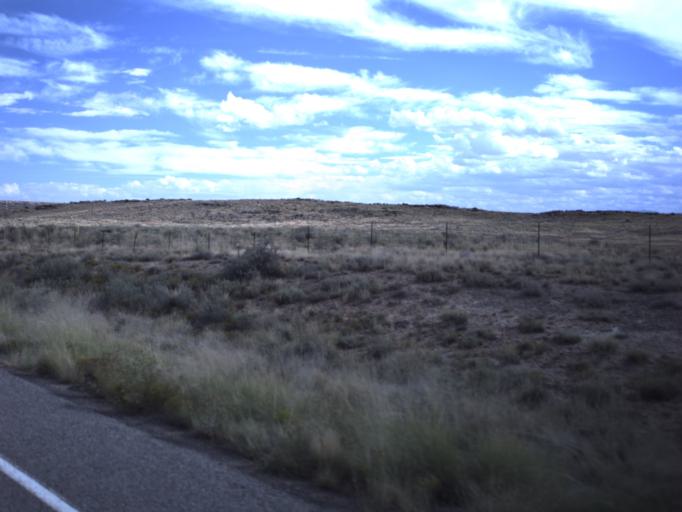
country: US
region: Colorado
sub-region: Montezuma County
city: Towaoc
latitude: 37.1673
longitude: -109.0813
